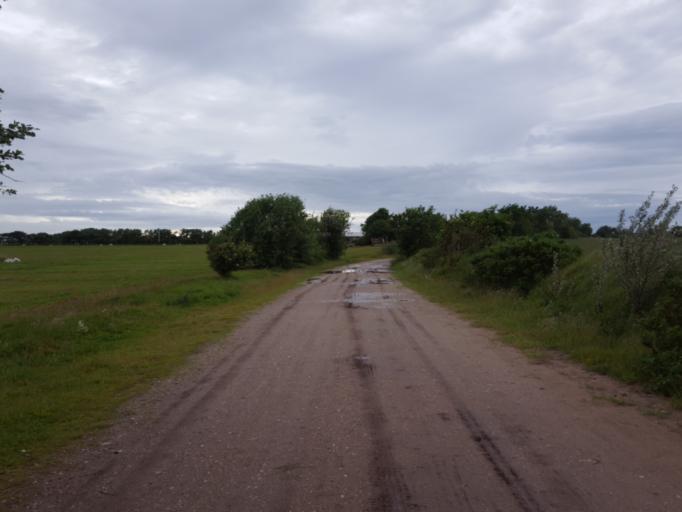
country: DE
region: Schleswig-Holstein
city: Nieblum
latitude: 54.6818
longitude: 8.5033
